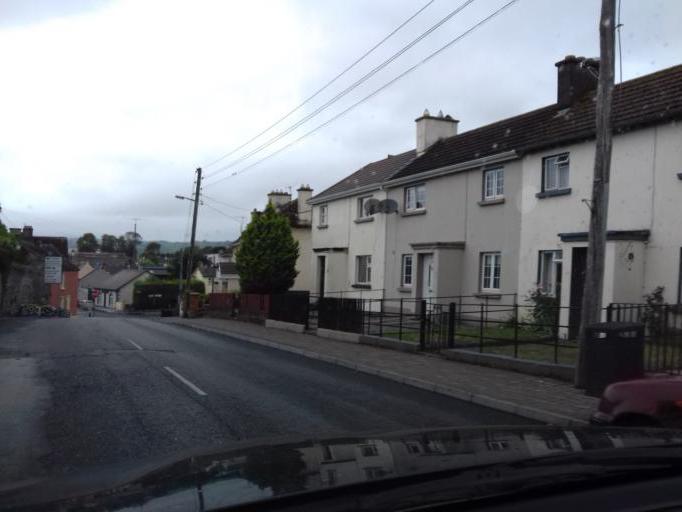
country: IE
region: Leinster
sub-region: County Carlow
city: Bagenalstown
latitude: 52.7358
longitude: -6.9747
